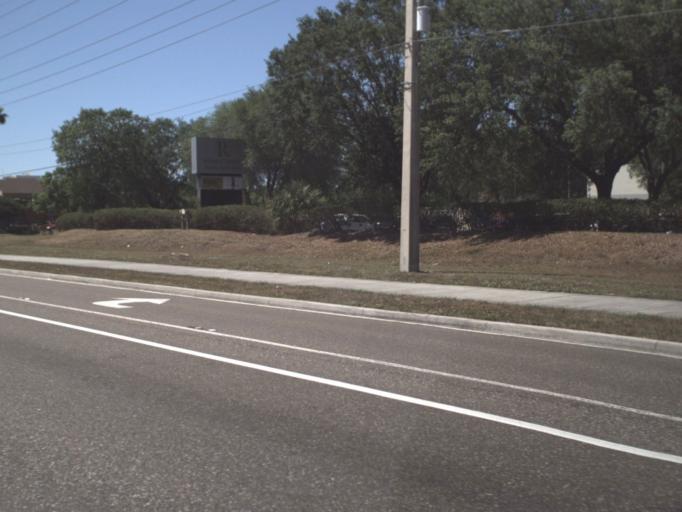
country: US
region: Florida
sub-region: Orange County
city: Conway
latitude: 28.4618
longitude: -81.3102
